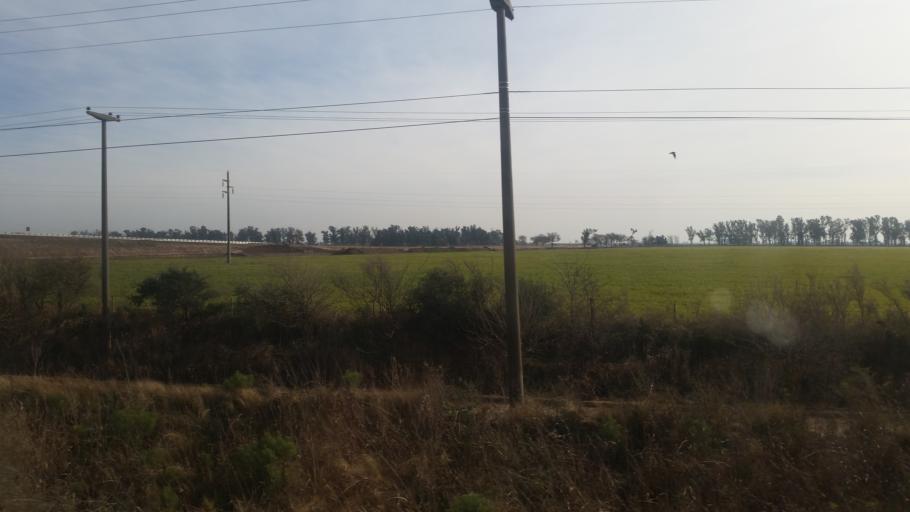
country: AR
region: Cordoba
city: Bell Ville
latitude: -32.6148
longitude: -62.7136
